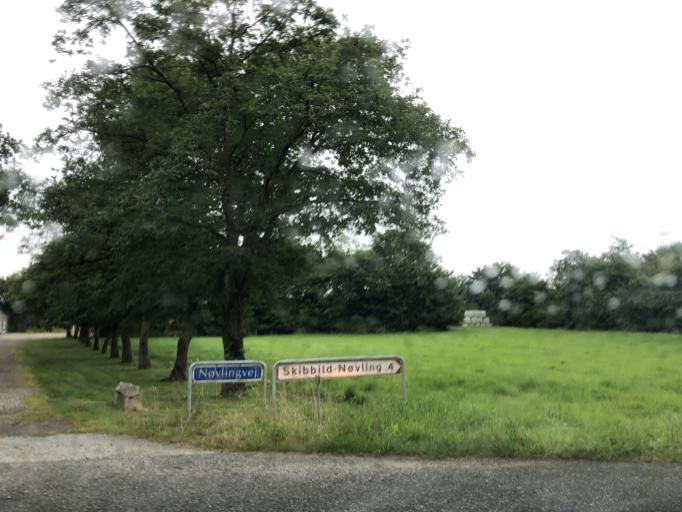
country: DK
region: Central Jutland
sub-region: Herning Kommune
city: Avlum
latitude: 56.2072
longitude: 8.8453
